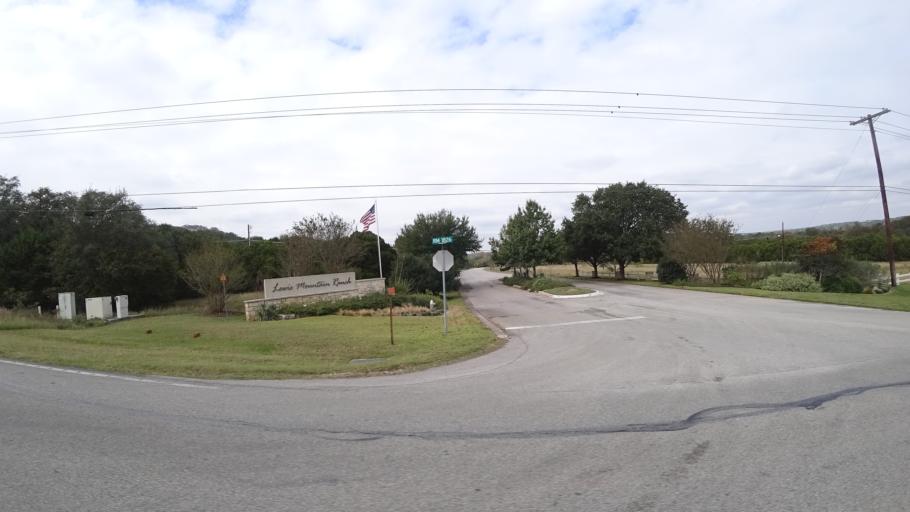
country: US
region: Texas
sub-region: Travis County
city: Shady Hollow
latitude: 30.2059
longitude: -97.9111
